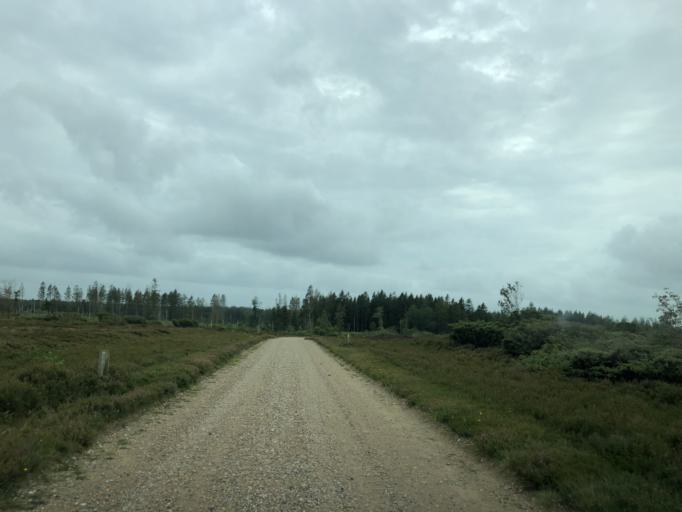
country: DK
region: Central Jutland
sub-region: Holstebro Kommune
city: Holstebro
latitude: 56.2409
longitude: 8.4928
